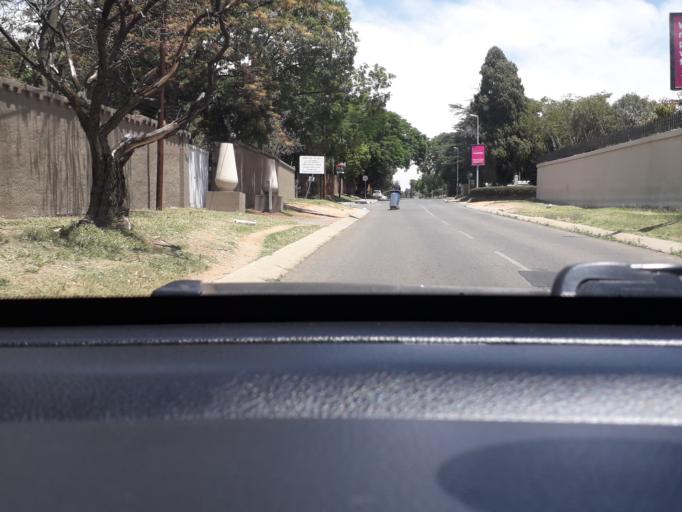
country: ZA
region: Gauteng
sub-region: City of Johannesburg Metropolitan Municipality
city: Modderfontein
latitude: -26.0991
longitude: 28.0701
